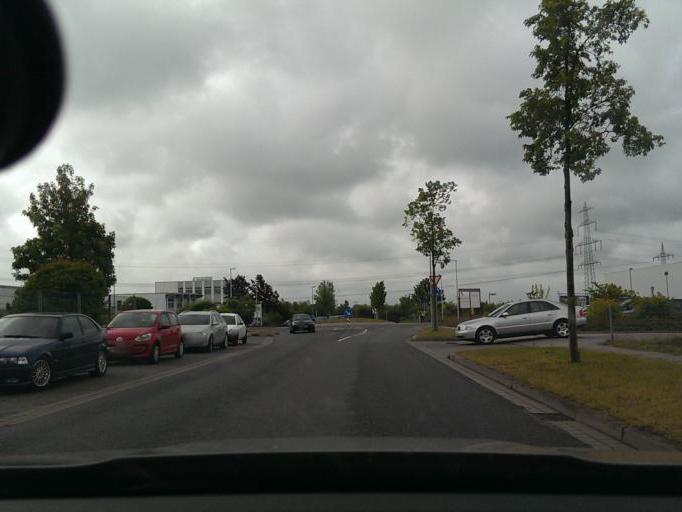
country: DE
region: Lower Saxony
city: Wolfsburg
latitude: 52.3708
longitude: 10.7382
